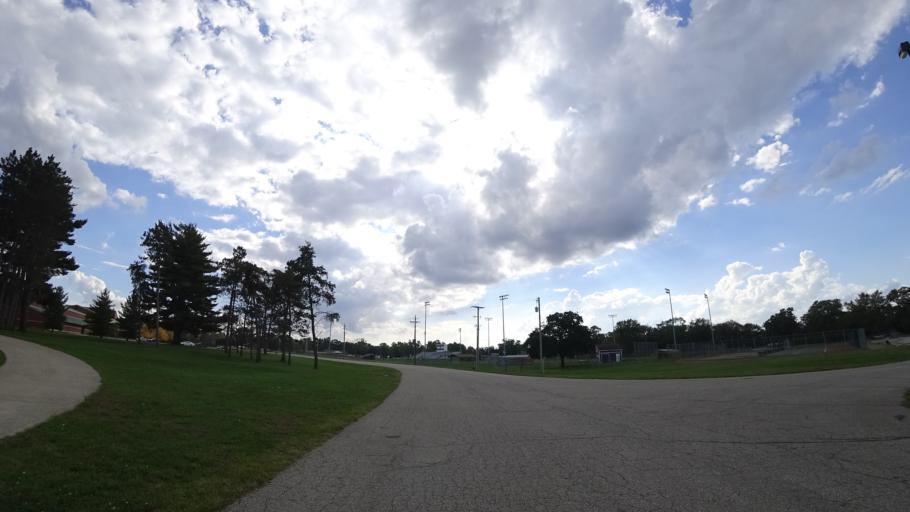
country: US
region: Michigan
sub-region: Saint Joseph County
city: Three Rivers
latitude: 41.9513
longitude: -85.6171
